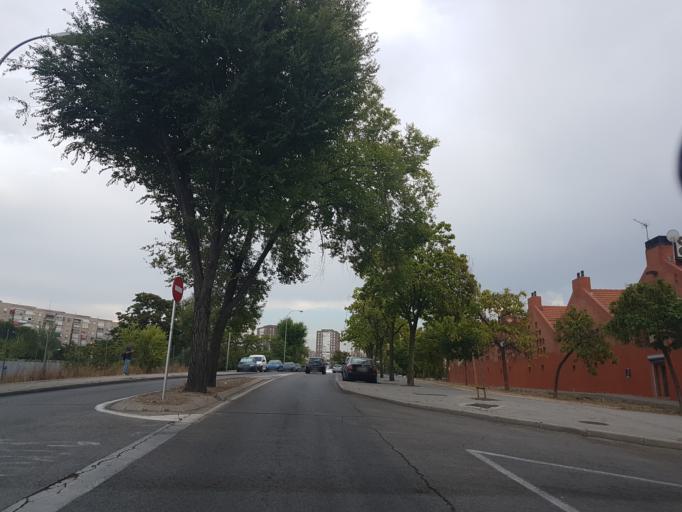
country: ES
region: Madrid
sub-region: Provincia de Madrid
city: Puente de Vallecas
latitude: 40.4053
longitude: -3.6579
